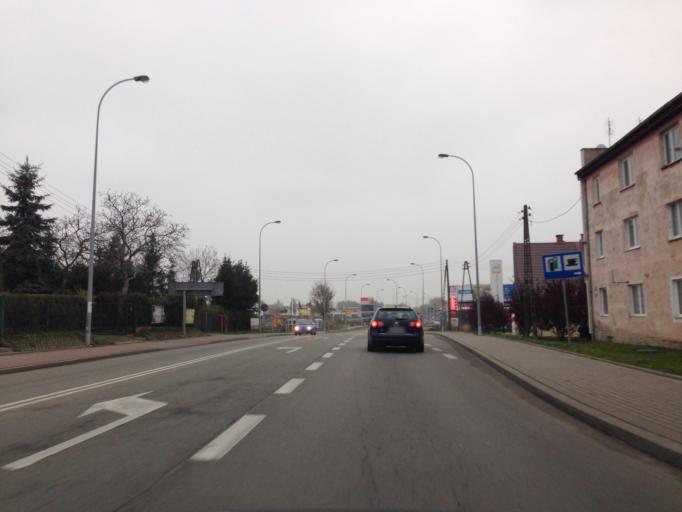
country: PL
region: Pomeranian Voivodeship
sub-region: Powiat gdanski
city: Pruszcz Gdanski
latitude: 54.2494
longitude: 18.6328
